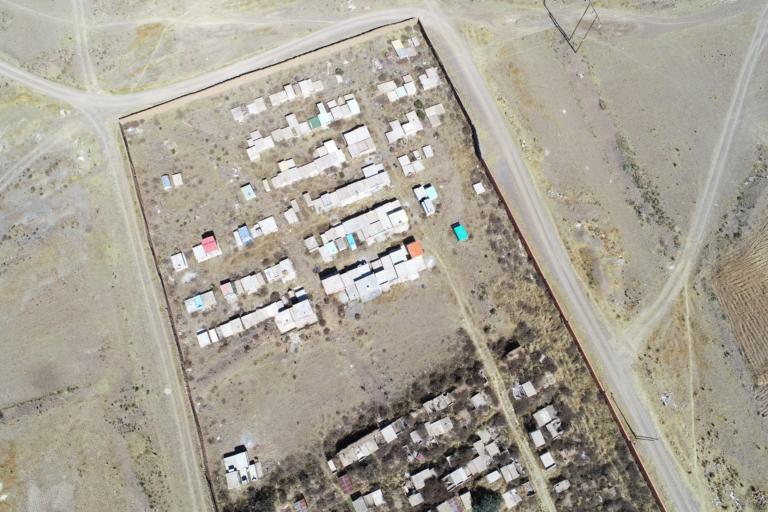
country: BO
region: La Paz
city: Achacachi
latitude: -15.9005
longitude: -68.9064
